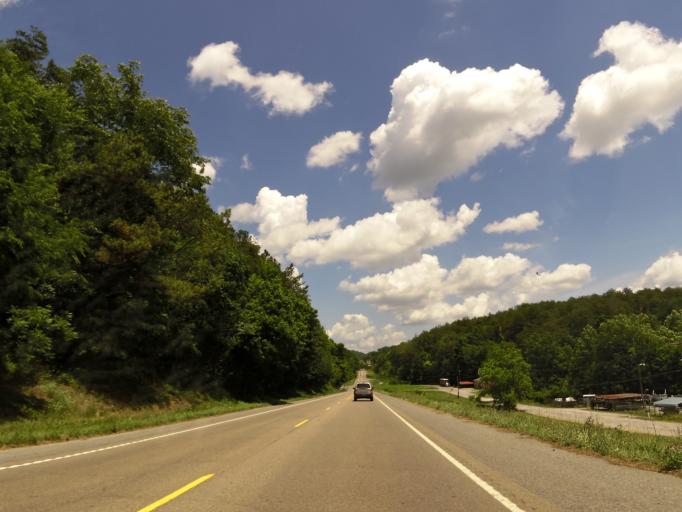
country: US
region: Tennessee
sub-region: Union County
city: Condon
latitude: 36.1756
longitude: -83.9027
